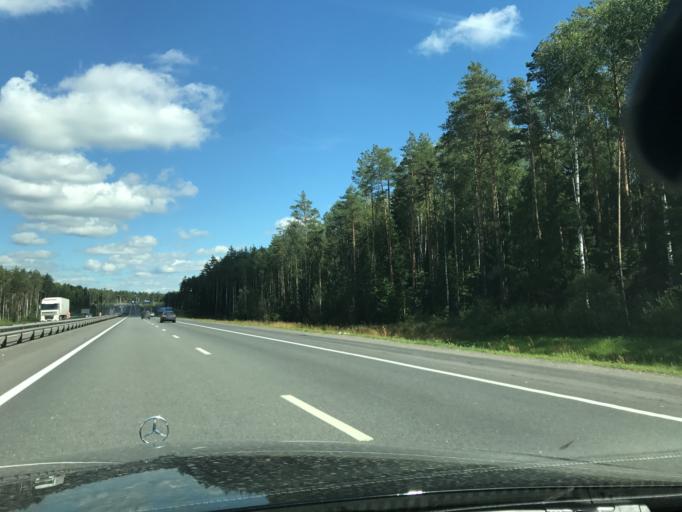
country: RU
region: Vladimir
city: Kameshkovo
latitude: 56.1865
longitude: 40.9491
